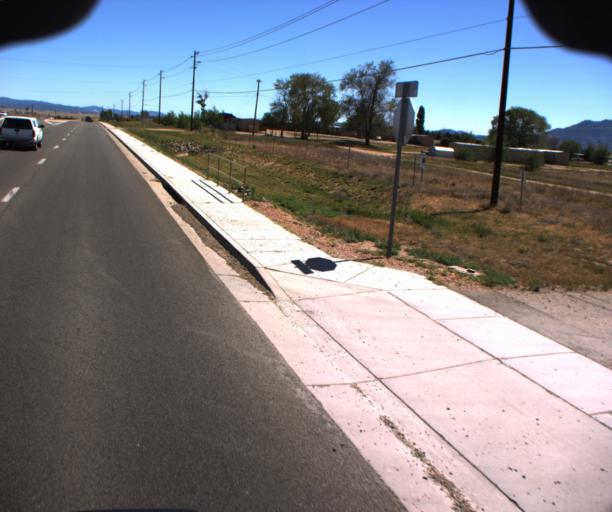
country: US
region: Arizona
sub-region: Yavapai County
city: Chino Valley
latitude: 34.7220
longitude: -112.4538
